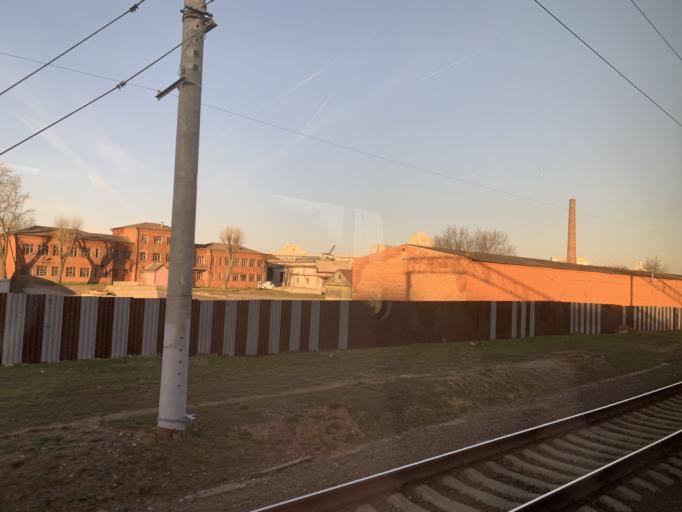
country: BY
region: Minsk
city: Minsk
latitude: 53.8944
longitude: 27.5345
